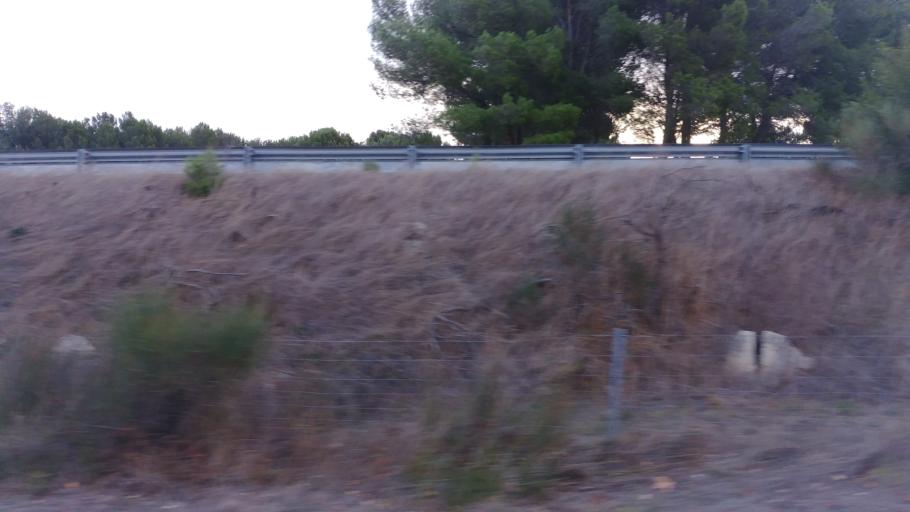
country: FR
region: Provence-Alpes-Cote d'Azur
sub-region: Departement des Bouches-du-Rhone
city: Venelles
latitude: 43.5734
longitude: 5.4669
